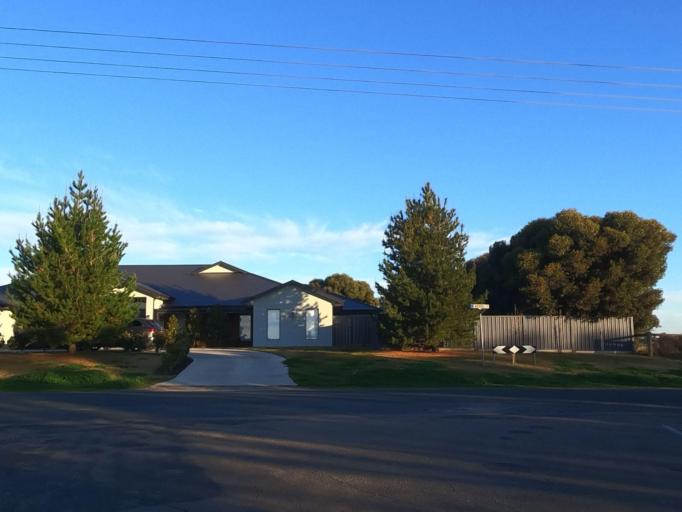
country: AU
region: Victoria
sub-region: Swan Hill
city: Swan Hill
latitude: -35.3605
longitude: 143.5517
